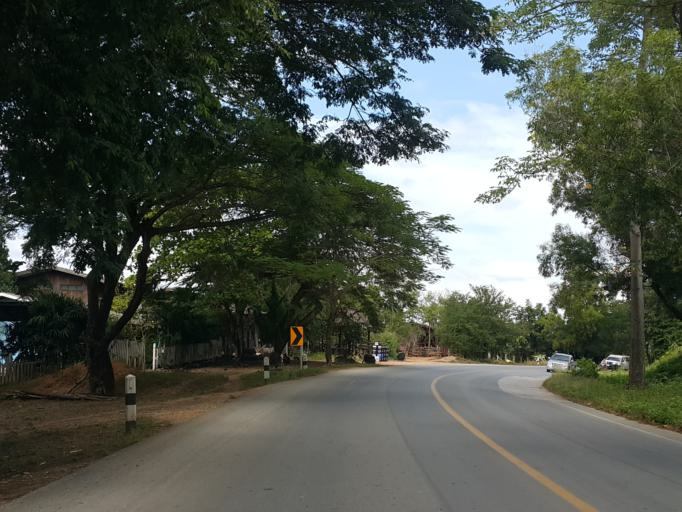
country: TH
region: Lampang
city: Hang Chat
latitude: 18.4311
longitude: 99.4442
